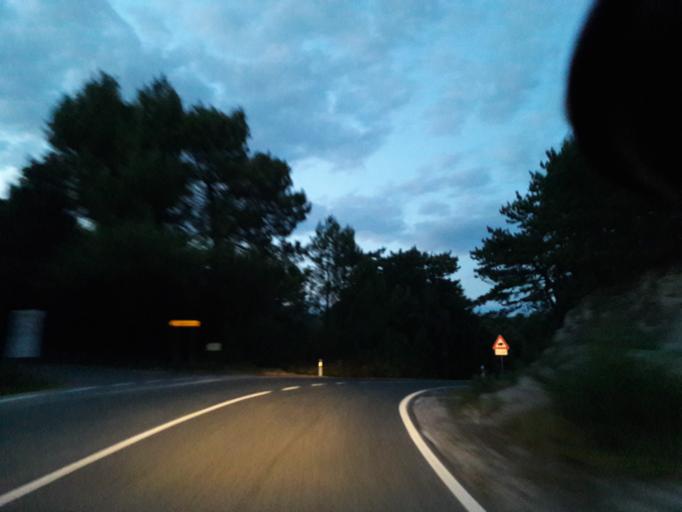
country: HR
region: Dubrovacko-Neretvanska
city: Orebic
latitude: 42.9715
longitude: 17.2959
